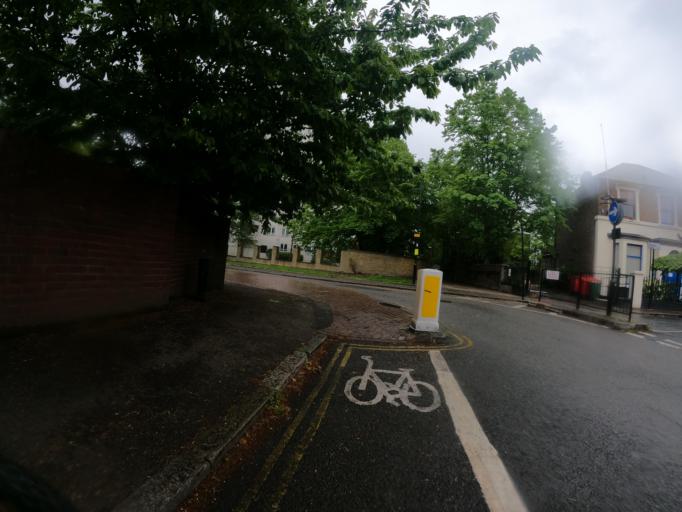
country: GB
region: England
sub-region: Greater London
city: Acton
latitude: 51.5055
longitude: -0.2739
